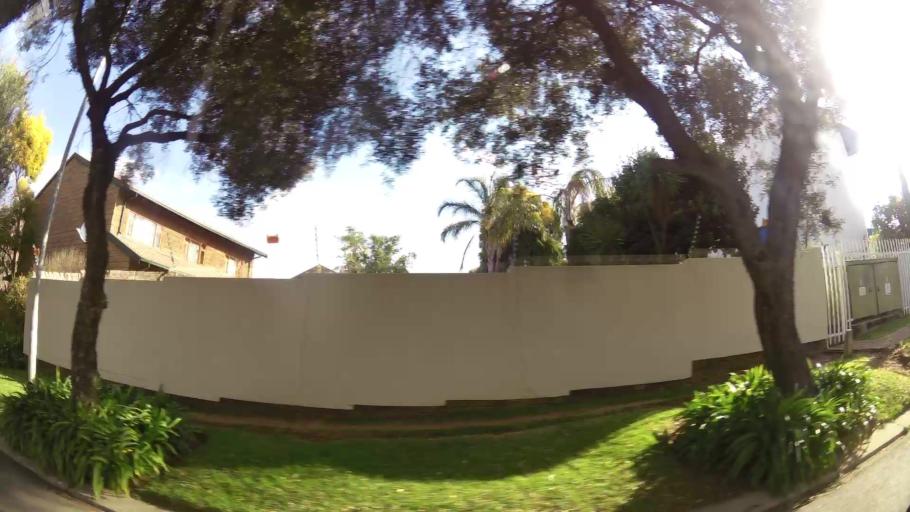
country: ZA
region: Gauteng
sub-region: City of Johannesburg Metropolitan Municipality
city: Diepsloot
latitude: -26.0118
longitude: 28.0304
